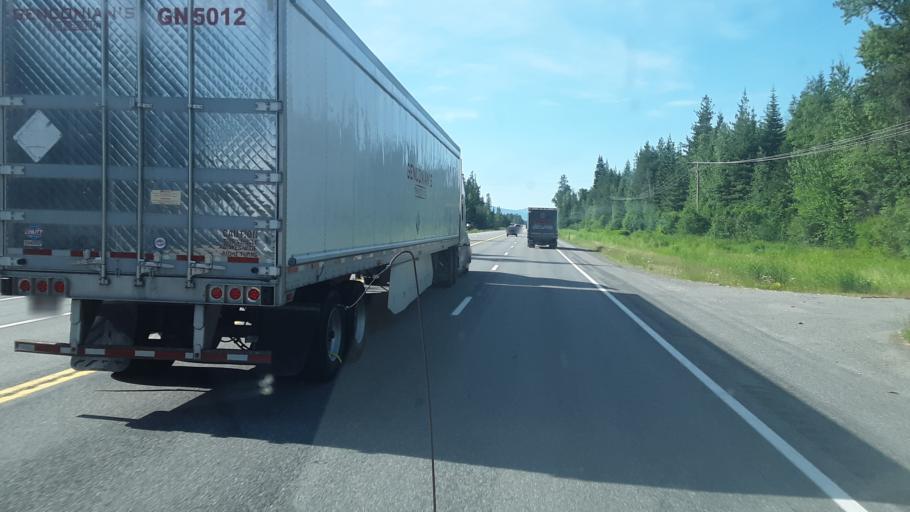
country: US
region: Idaho
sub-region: Bonner County
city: Ponderay
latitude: 48.3635
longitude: -116.5478
